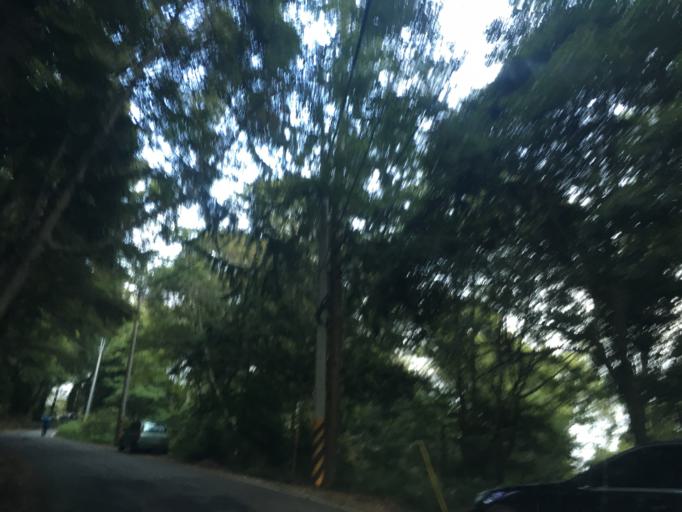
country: TW
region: Taiwan
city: Fengyuan
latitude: 24.2338
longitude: 120.9813
